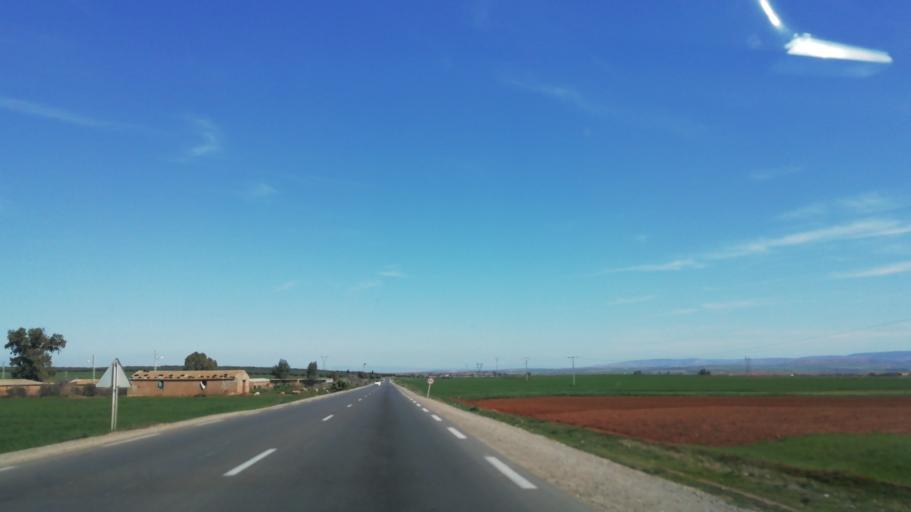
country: DZ
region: Mascara
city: Mascara
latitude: 35.4181
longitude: 0.4138
